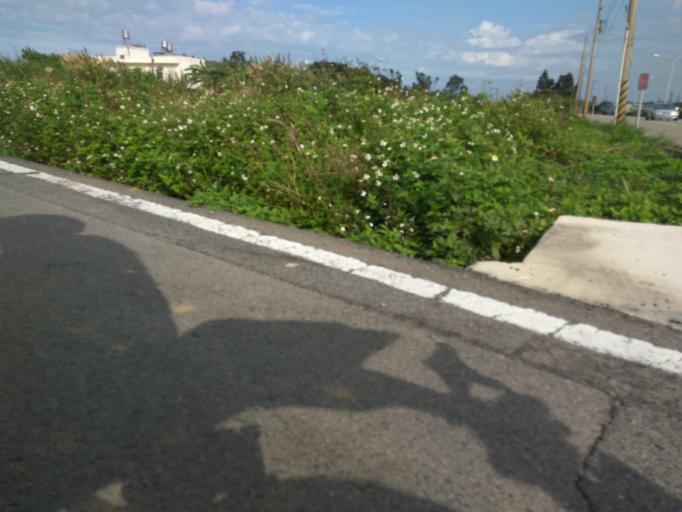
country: TW
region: Taiwan
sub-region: Hsinchu
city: Zhubei
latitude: 24.9626
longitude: 121.0144
